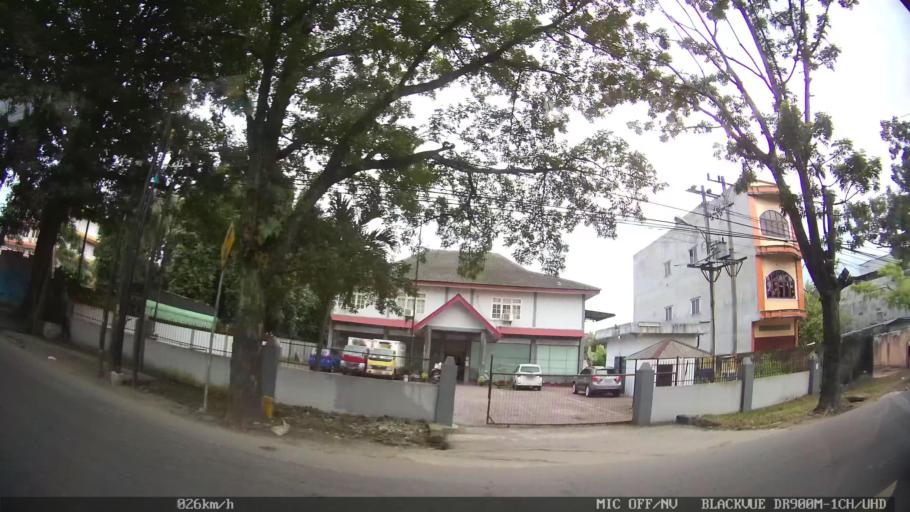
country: ID
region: North Sumatra
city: Deli Tua
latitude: 3.5413
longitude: 98.6638
